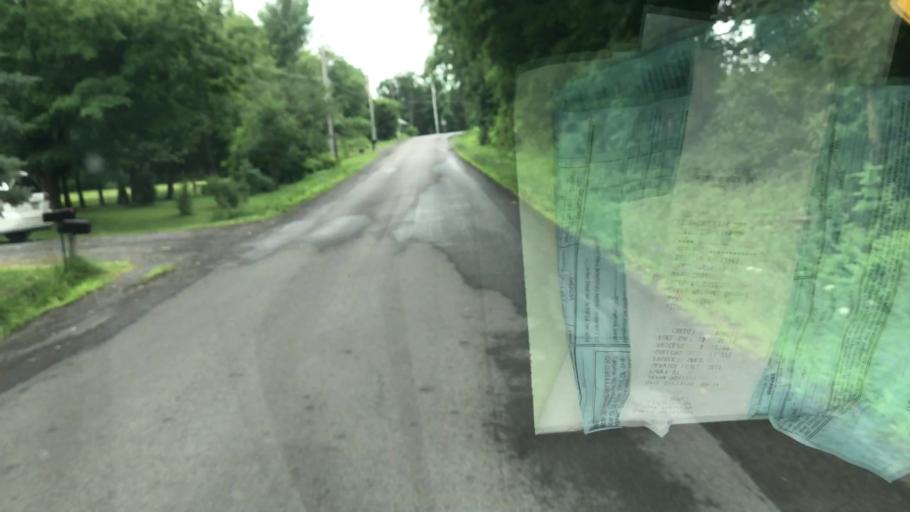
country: US
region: New York
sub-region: Onondaga County
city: Manlius
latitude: 42.9805
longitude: -75.9830
